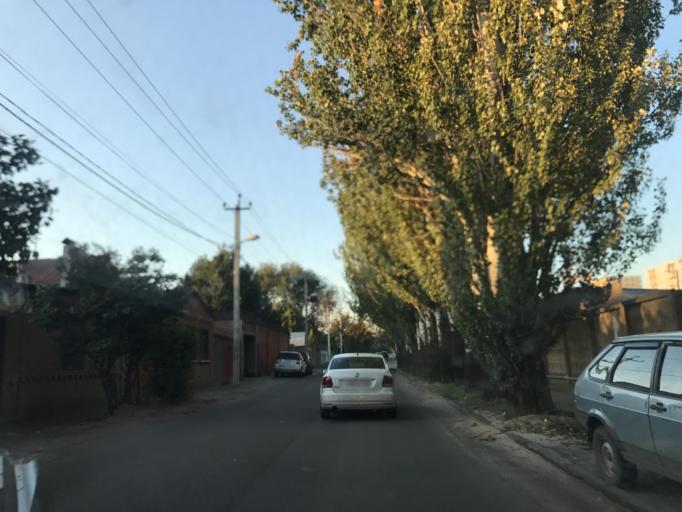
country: RU
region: Rostov
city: Imeni Chkalova
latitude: 47.2376
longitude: 39.7749
